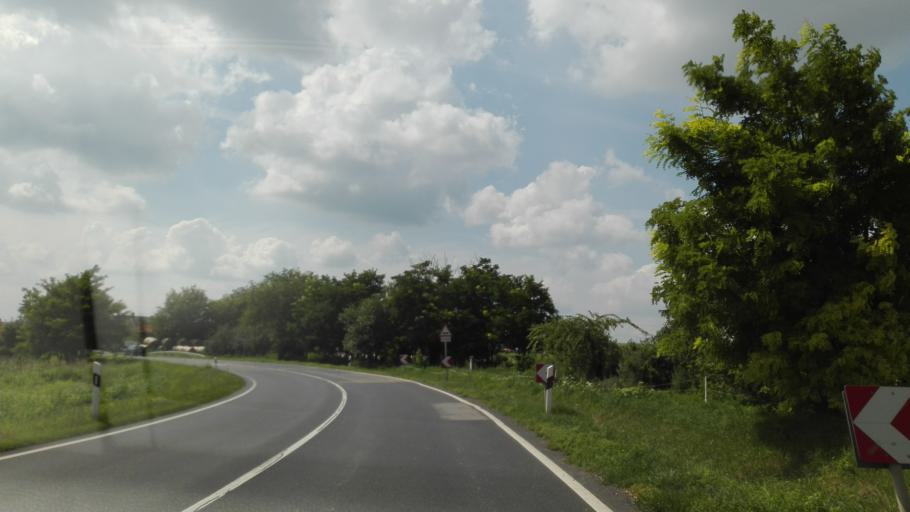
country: HU
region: Fejer
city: Alap
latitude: 46.7993
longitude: 18.7413
